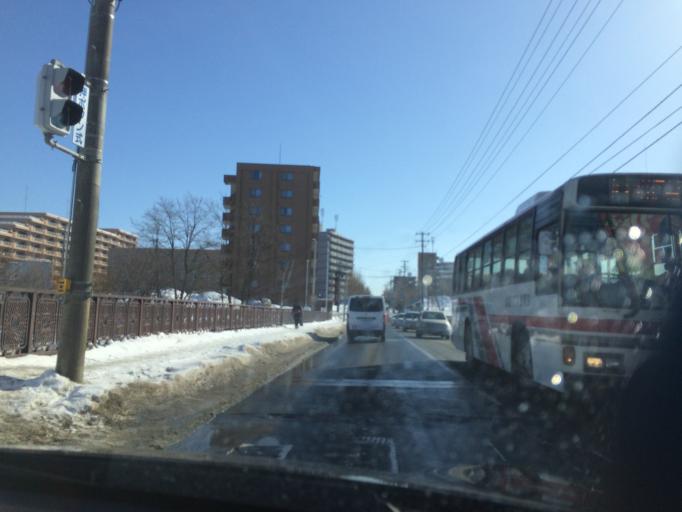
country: JP
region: Hokkaido
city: Sapporo
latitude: 43.0225
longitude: 141.4430
